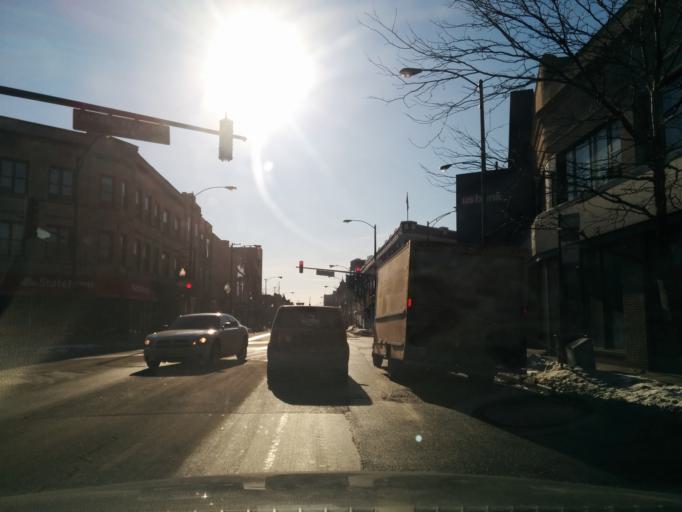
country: US
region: Illinois
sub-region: Cook County
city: Lincolnwood
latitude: 41.9352
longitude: -87.7175
